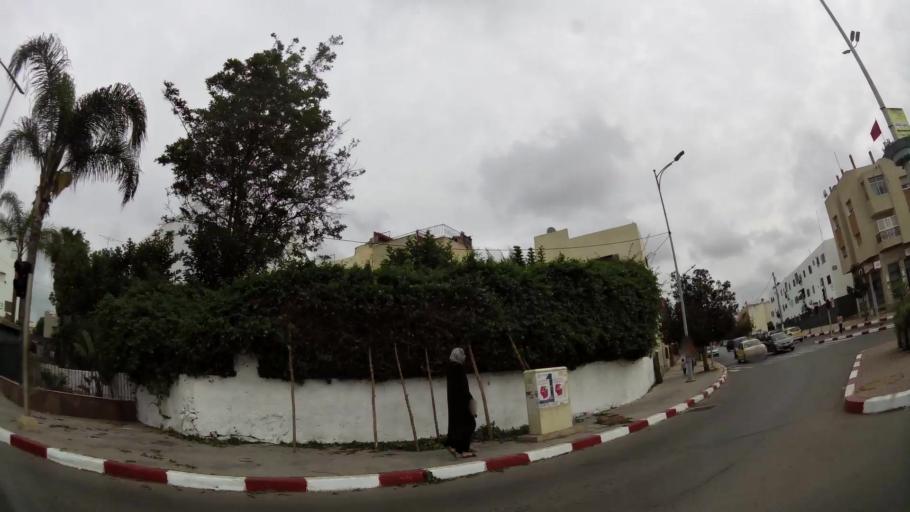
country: MA
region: Rabat-Sale-Zemmour-Zaer
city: Sale
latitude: 34.0466
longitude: -6.8021
